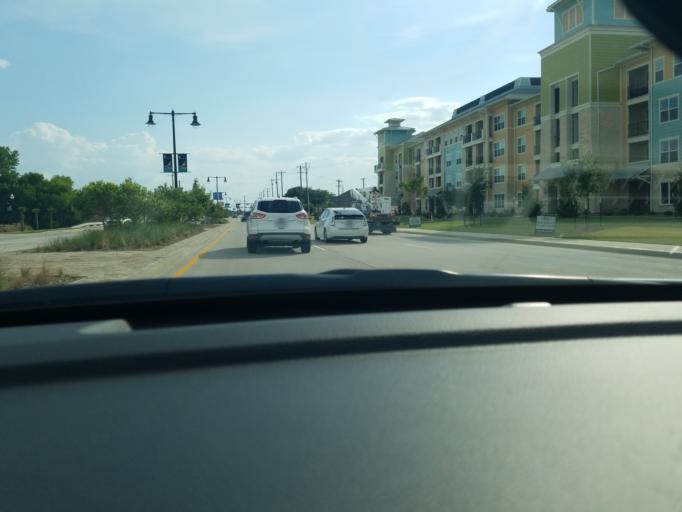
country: US
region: Texas
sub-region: Denton County
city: Little Elm
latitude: 33.1615
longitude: -96.9363
